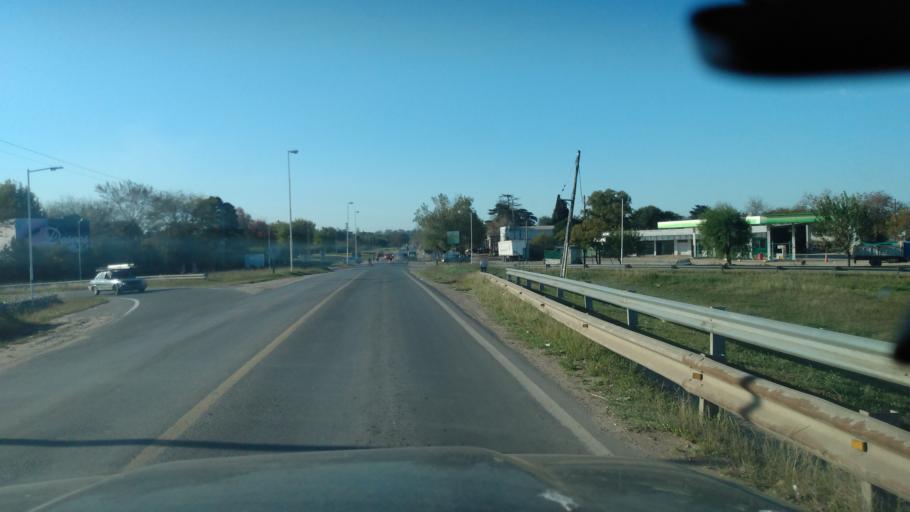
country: AR
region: Buenos Aires
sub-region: Partido de Lujan
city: Lujan
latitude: -34.5461
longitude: -59.1234
